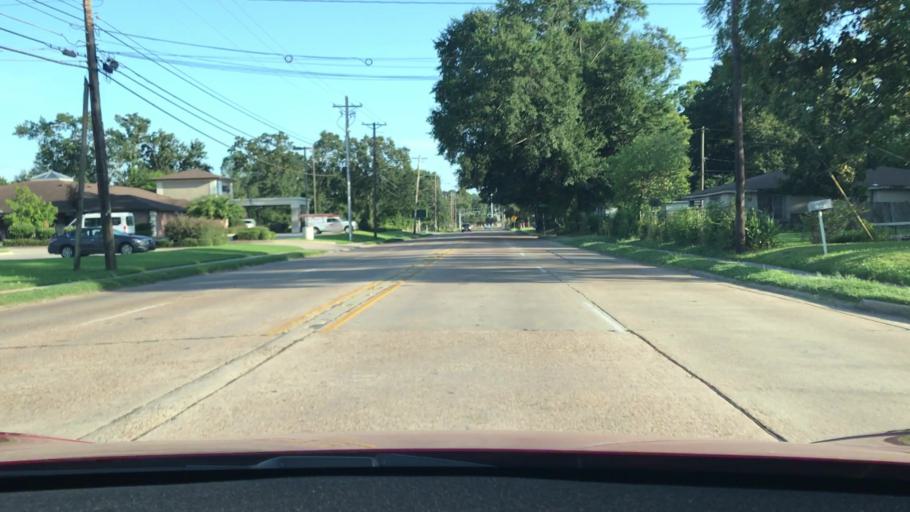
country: US
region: Louisiana
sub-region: Bossier Parish
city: Bossier City
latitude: 32.4362
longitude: -93.7460
